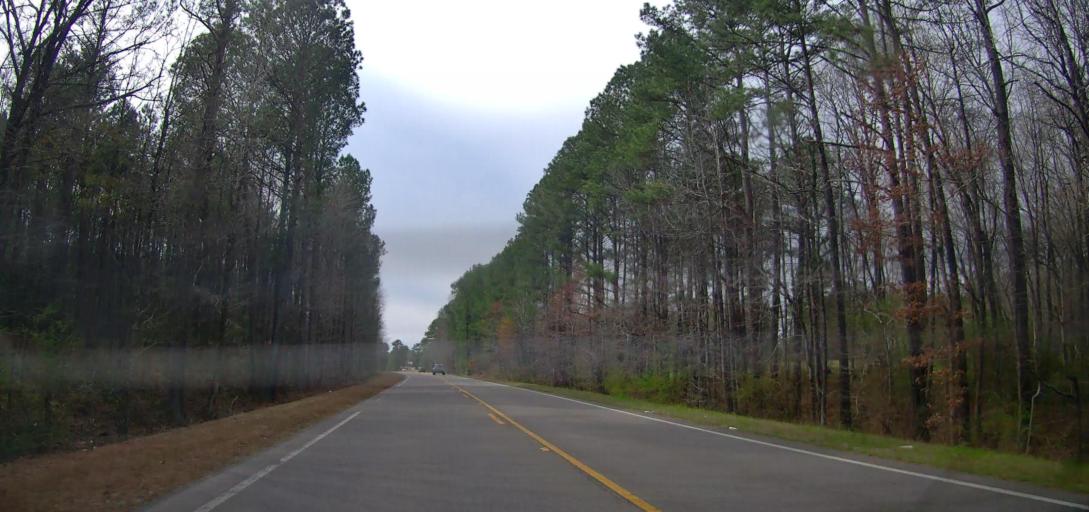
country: US
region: Alabama
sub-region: Walker County
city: Carbon Hill
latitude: 33.8763
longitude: -87.4702
